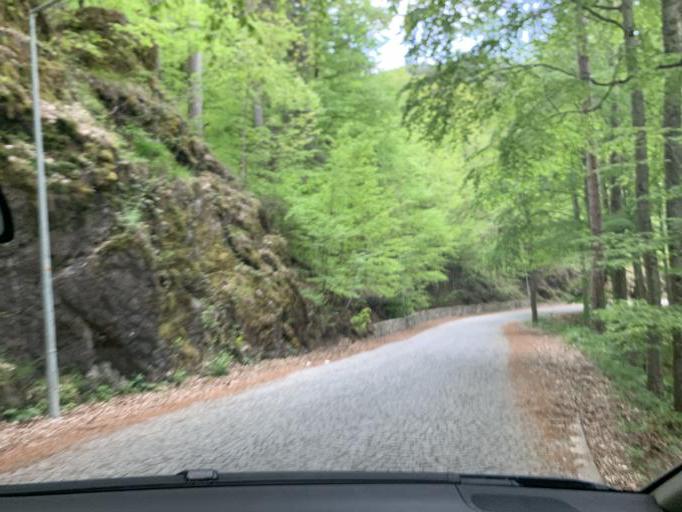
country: TR
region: Zonguldak
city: Egerci
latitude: 40.9364
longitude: 31.7409
